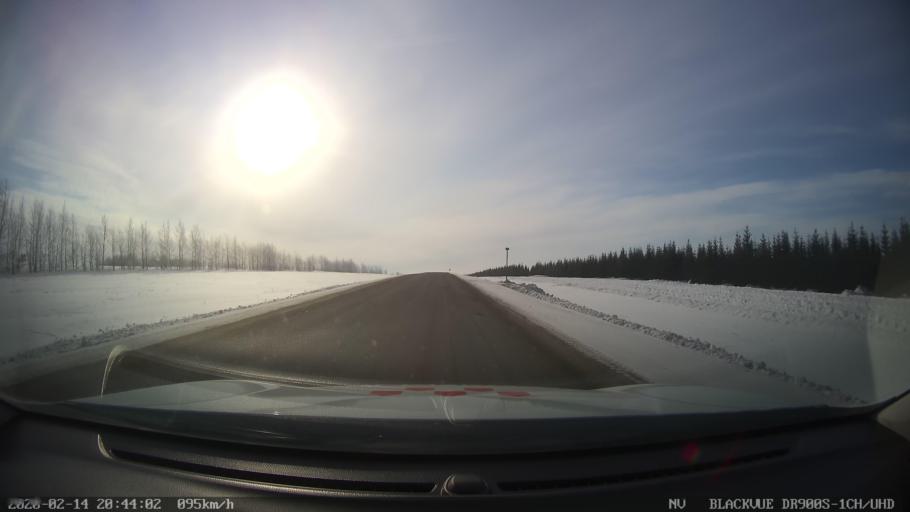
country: RU
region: Tatarstan
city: Kuybyshevskiy Zaton
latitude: 55.3000
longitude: 49.1472
